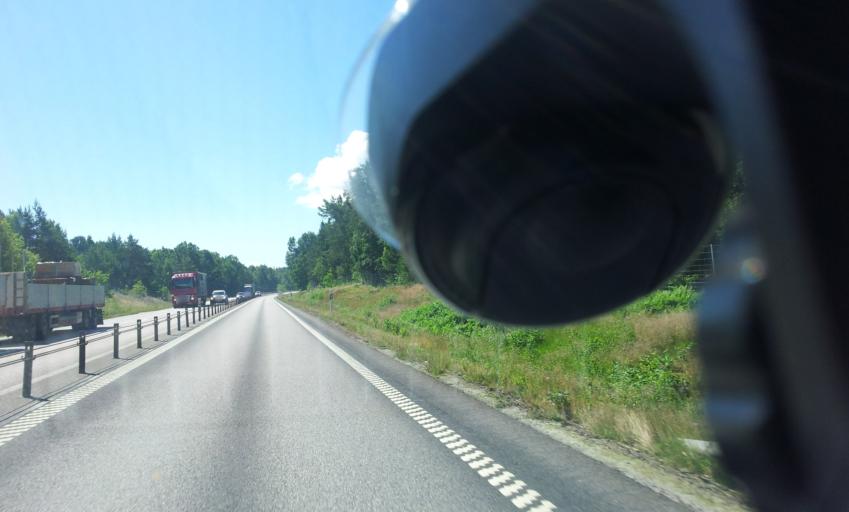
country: SE
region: Kalmar
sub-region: Oskarshamns Kommun
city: Paskallavik
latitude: 57.1865
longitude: 16.4418
